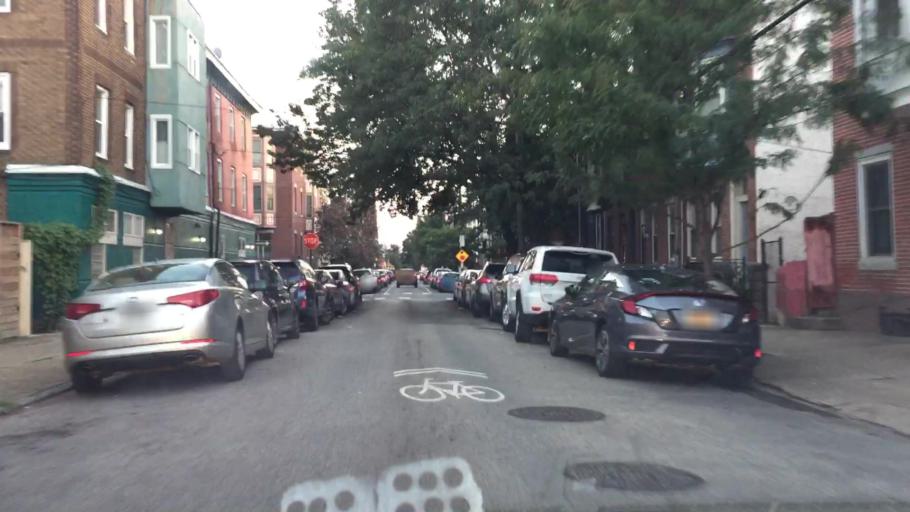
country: US
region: Pennsylvania
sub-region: Philadelphia County
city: Philadelphia
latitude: 39.9437
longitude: -75.1773
